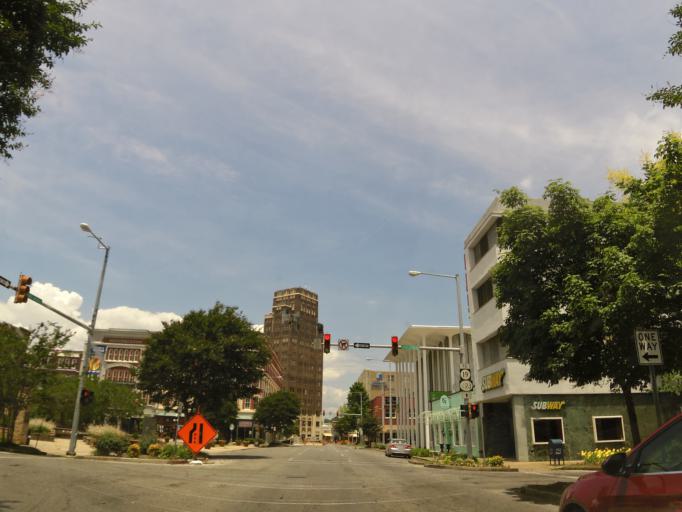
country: US
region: Mississippi
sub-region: Lauderdale County
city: Meridian
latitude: 32.3633
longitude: -88.6993
